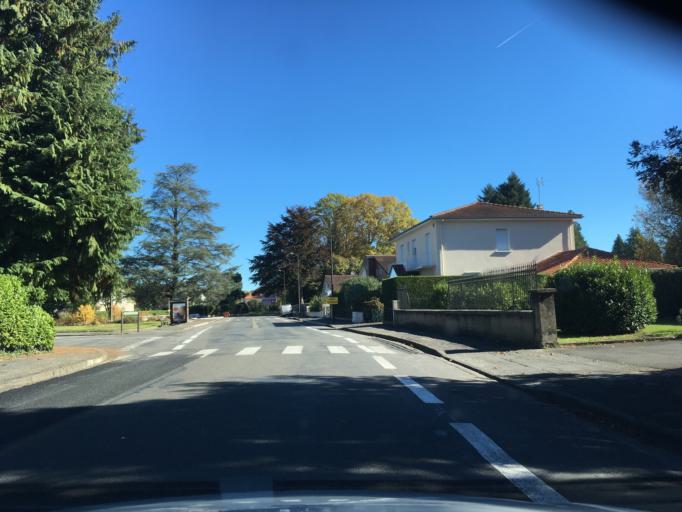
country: FR
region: Aquitaine
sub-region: Departement des Pyrenees-Atlantiques
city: Bizanos
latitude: 43.2985
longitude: -0.3359
